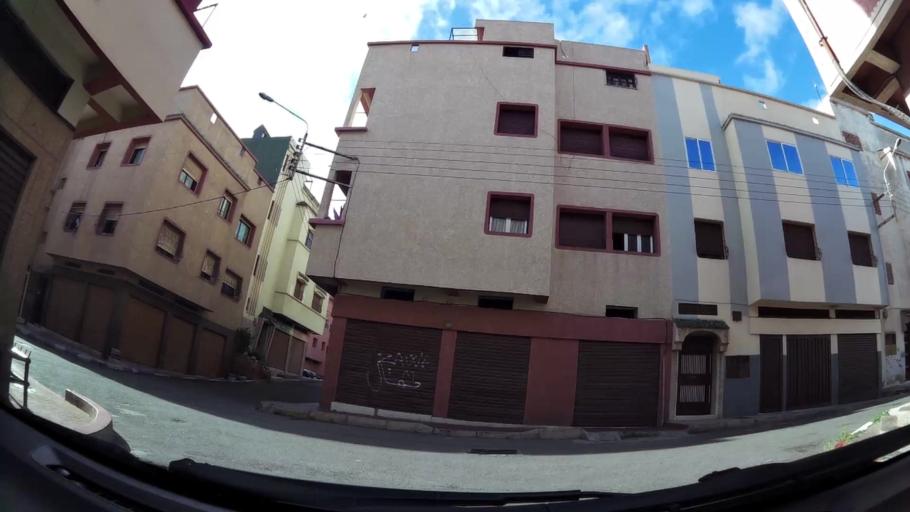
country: MA
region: Grand Casablanca
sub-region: Casablanca
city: Casablanca
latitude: 33.5427
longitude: -7.5931
